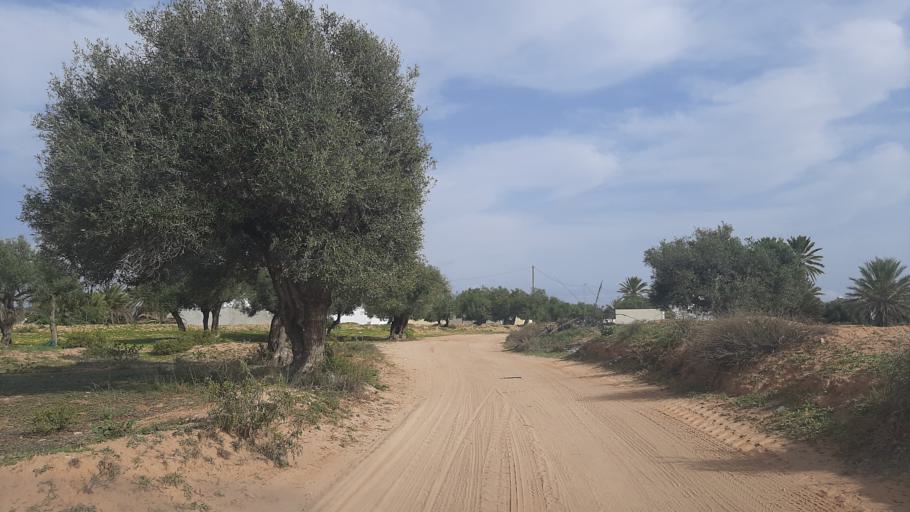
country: TN
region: Madanin
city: Midoun
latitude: 33.8092
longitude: 11.0244
